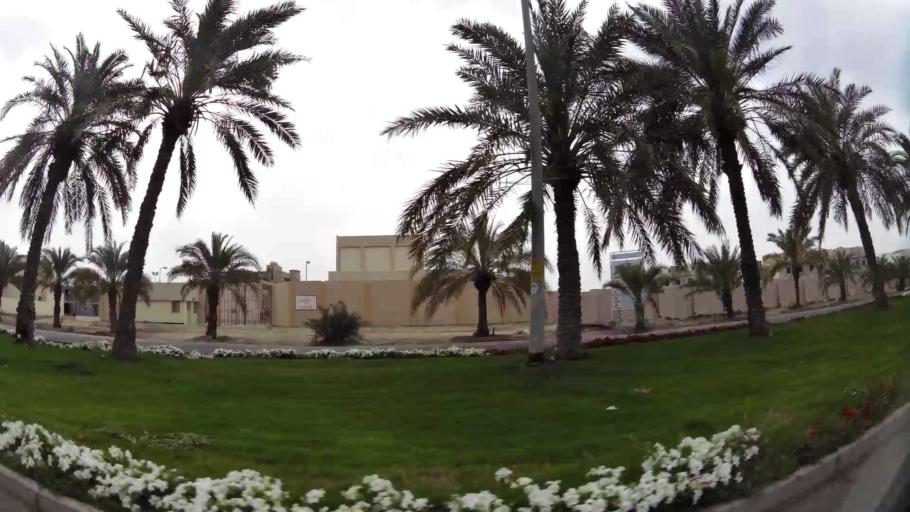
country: BH
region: Central Governorate
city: Dar Kulayb
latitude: 26.0550
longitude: 50.4901
